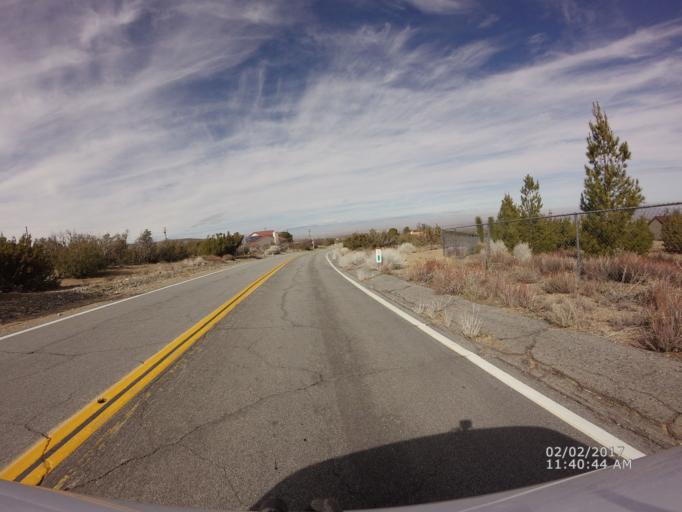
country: US
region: California
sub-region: Los Angeles County
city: Littlerock
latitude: 34.4414
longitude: -117.9348
